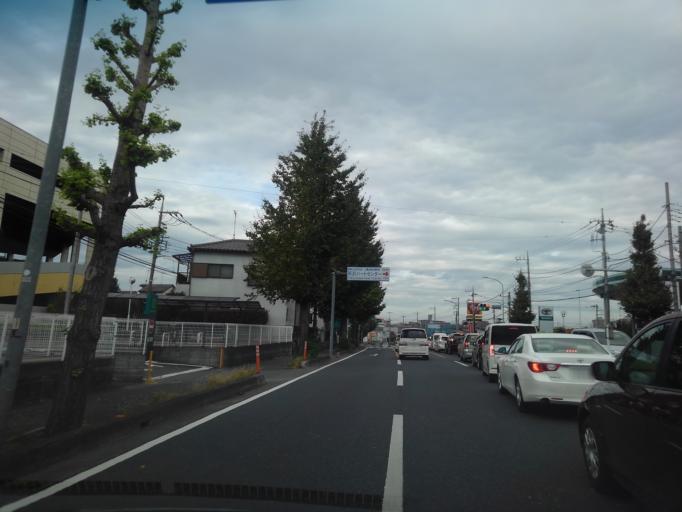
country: JP
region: Saitama
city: Tokorozawa
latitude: 35.7920
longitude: 139.4438
